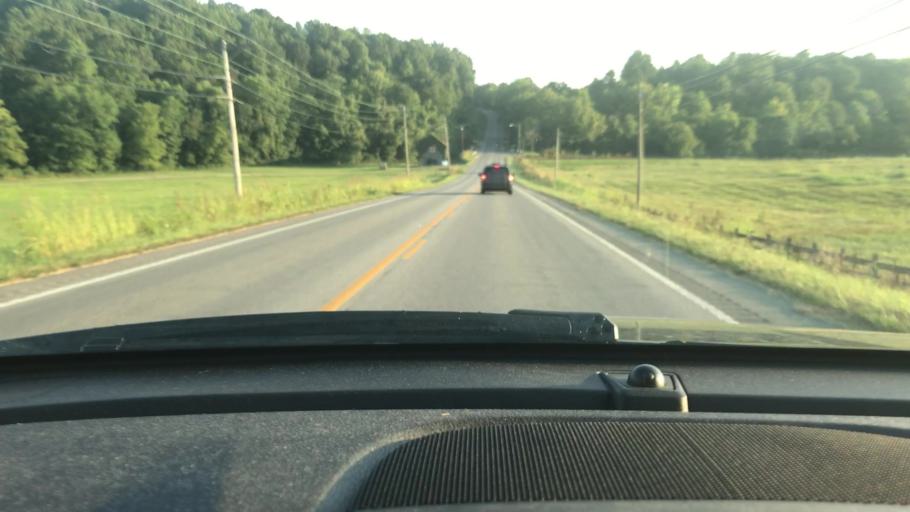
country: US
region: Tennessee
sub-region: Dickson County
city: Charlotte
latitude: 36.1642
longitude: -87.3528
